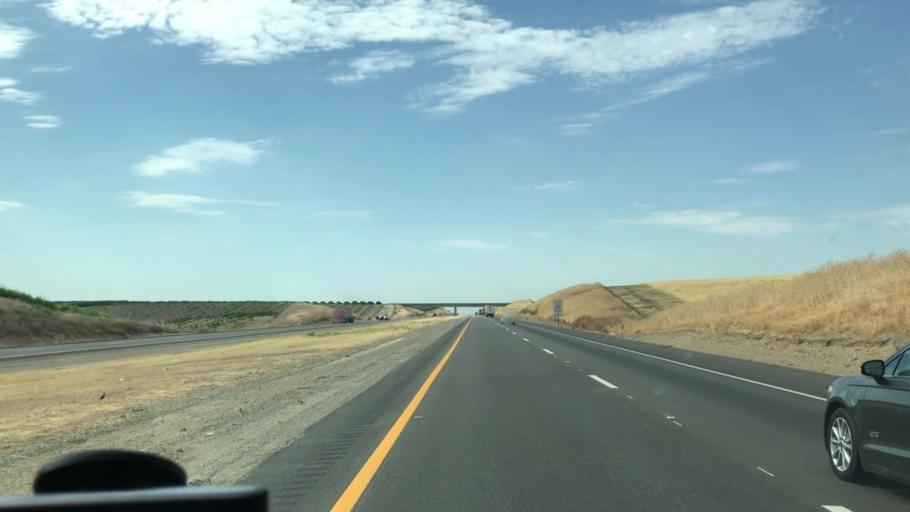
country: US
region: California
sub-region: Stanislaus County
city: Newman
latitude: 37.3580
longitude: -121.1207
